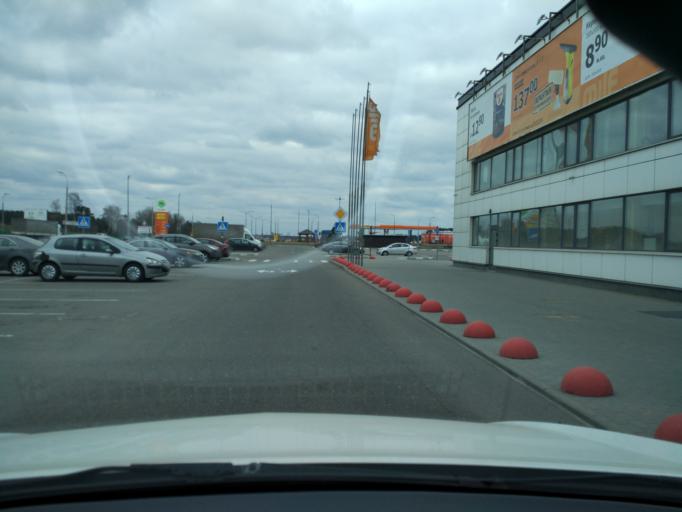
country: BY
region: Minsk
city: Bal'shavik
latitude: 53.9694
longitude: 27.5468
